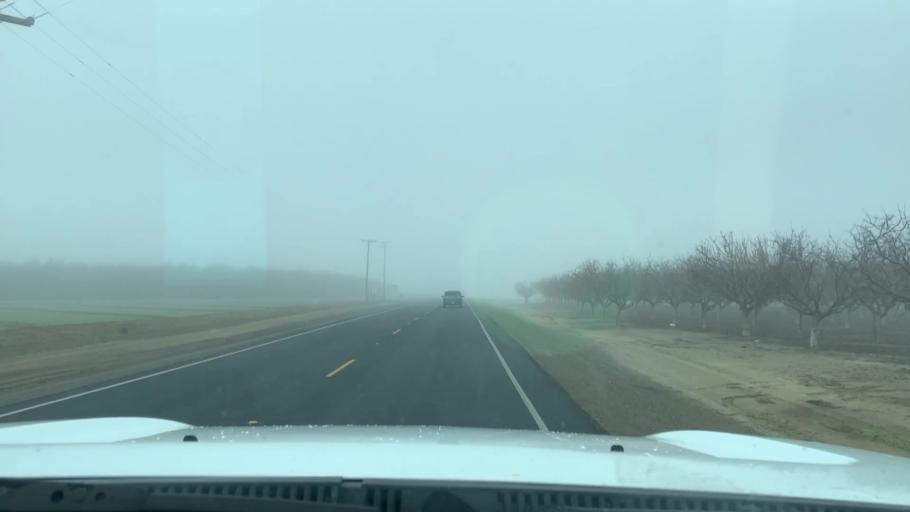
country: US
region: California
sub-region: Kern County
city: Lost Hills
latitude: 35.6085
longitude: -119.5817
